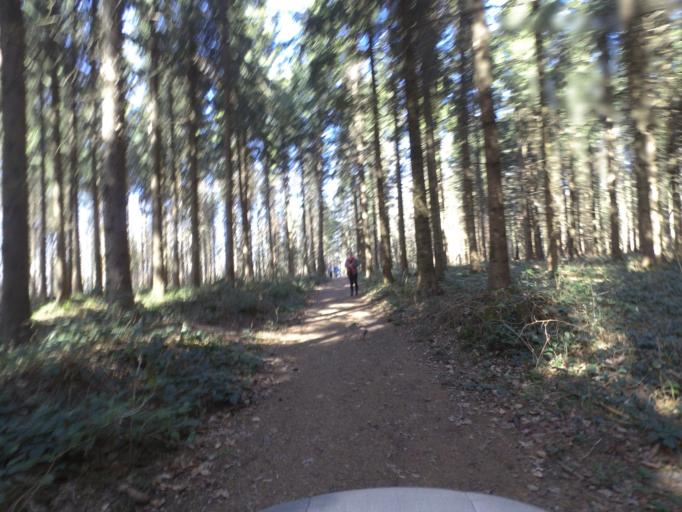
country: AT
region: Salzburg
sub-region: Politischer Bezirk Salzburg-Umgebung
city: Mattsee
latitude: 47.9894
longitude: 13.1009
